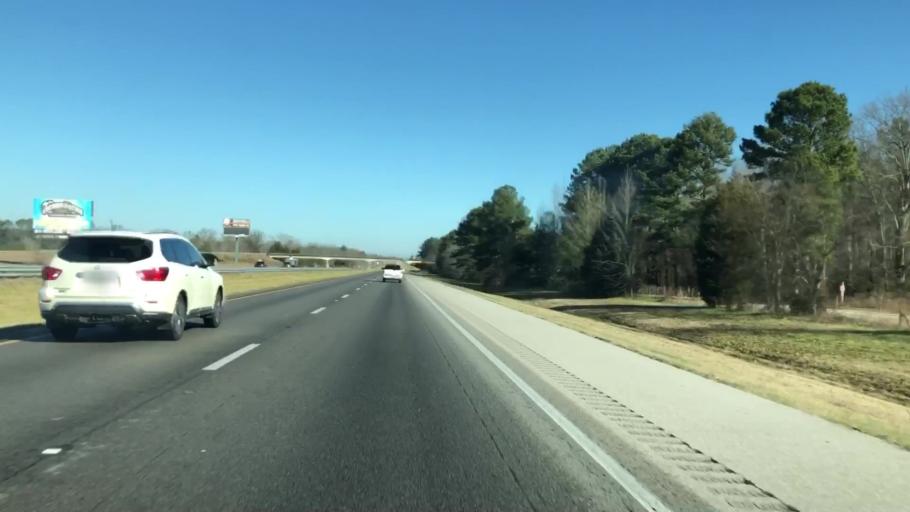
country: US
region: Alabama
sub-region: Limestone County
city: Athens
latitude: 34.8577
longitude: -86.9273
